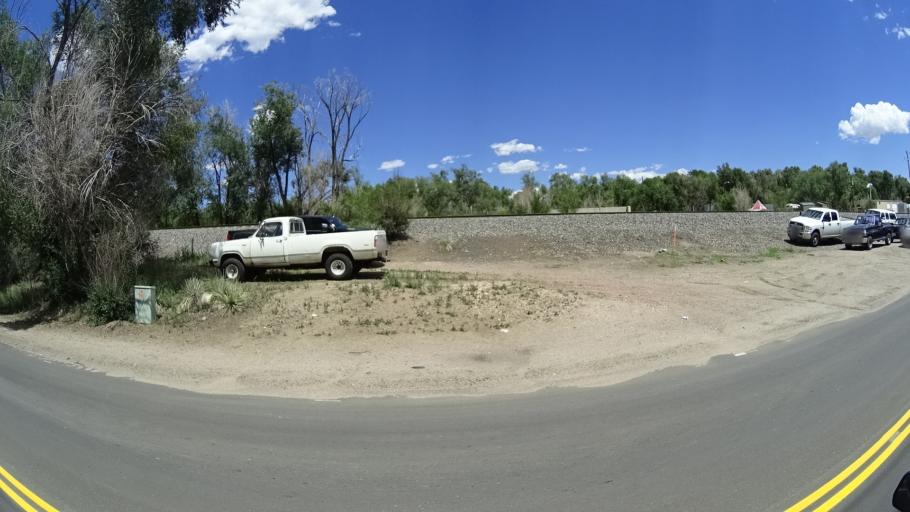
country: US
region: Colorado
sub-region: El Paso County
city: Colorado Springs
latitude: 38.8179
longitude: -104.8167
